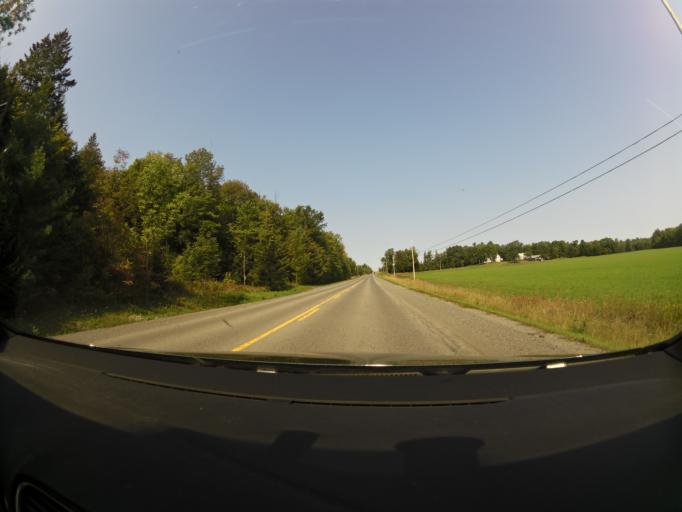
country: CA
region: Ontario
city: Arnprior
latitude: 45.3907
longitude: -76.1192
